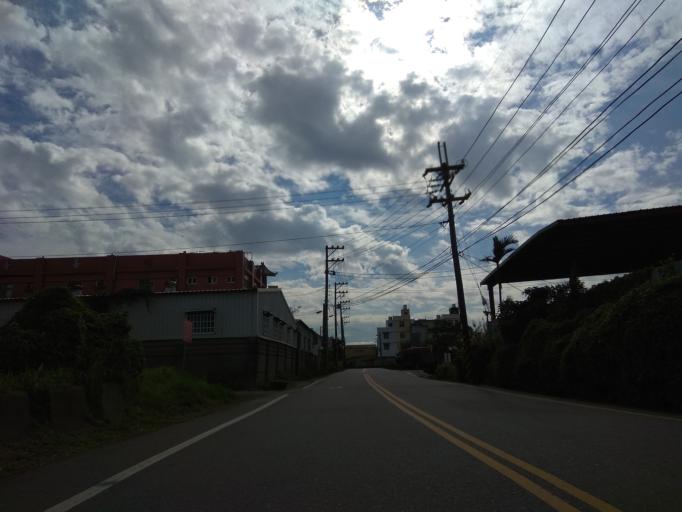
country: TW
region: Taiwan
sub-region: Hsinchu
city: Zhubei
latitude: 24.9566
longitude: 121.1102
